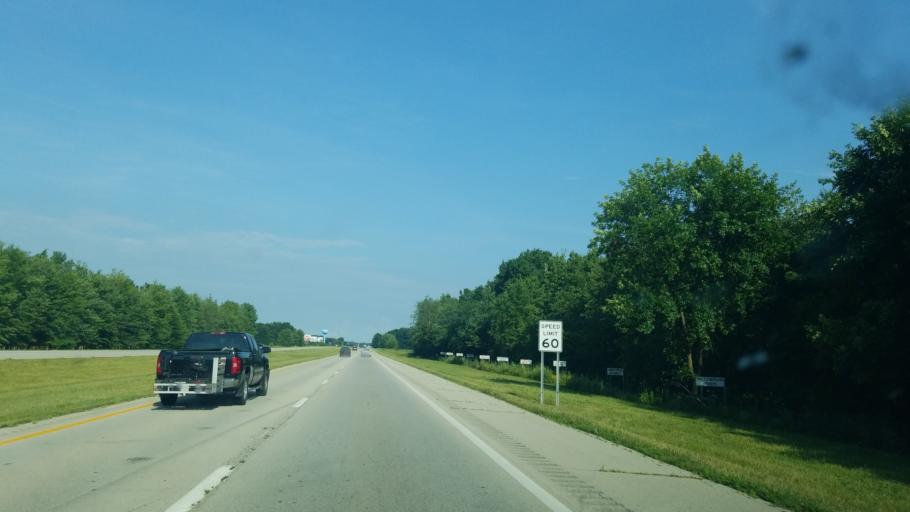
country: US
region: Ohio
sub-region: Brown County
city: Mount Orab
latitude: 39.0501
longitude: -83.9571
